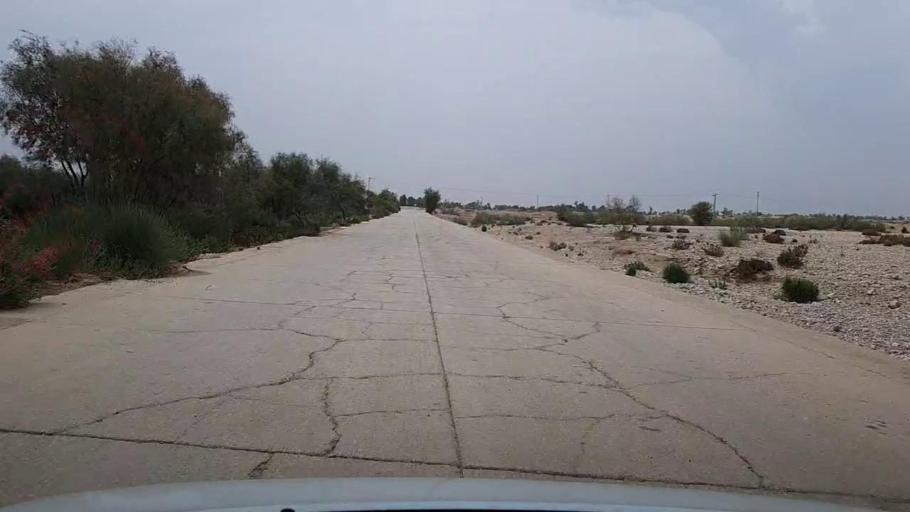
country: PK
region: Sindh
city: Sehwan
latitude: 26.3171
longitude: 67.7455
